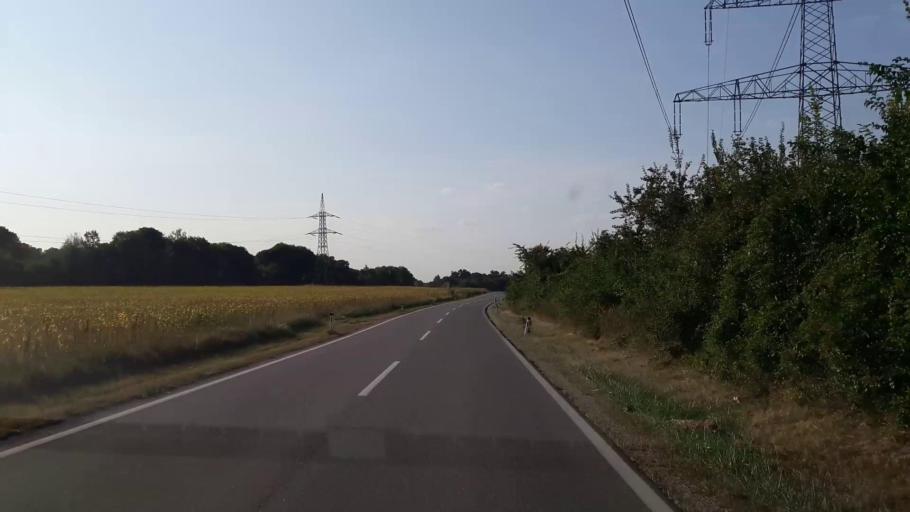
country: AT
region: Lower Austria
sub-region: Politischer Bezirk Ganserndorf
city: Orth an der Donau
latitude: 48.0819
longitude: 16.6774
